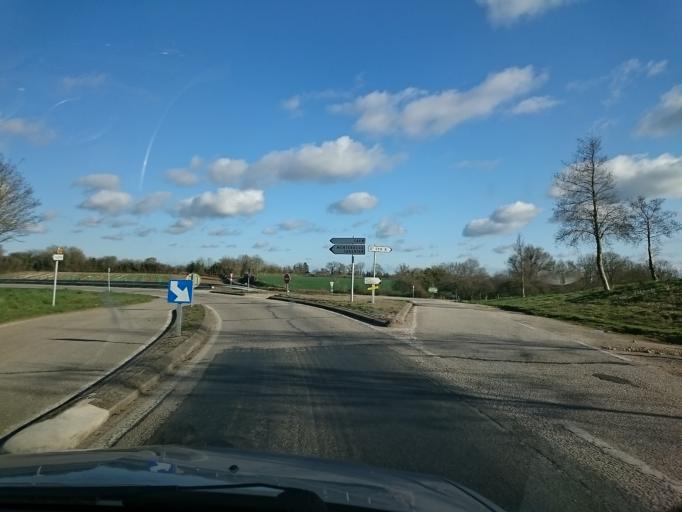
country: FR
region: Lower Normandy
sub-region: Departement de la Manche
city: Valognes
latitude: 49.4983
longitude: -1.4506
